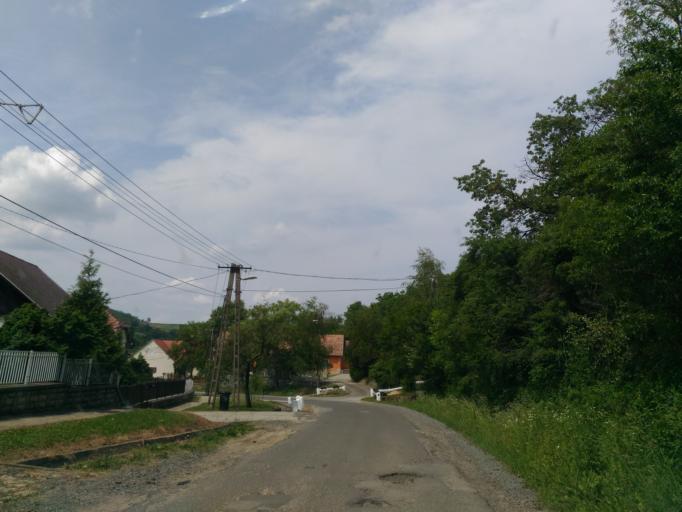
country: HU
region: Baranya
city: Komlo
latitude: 46.1945
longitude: 18.2311
